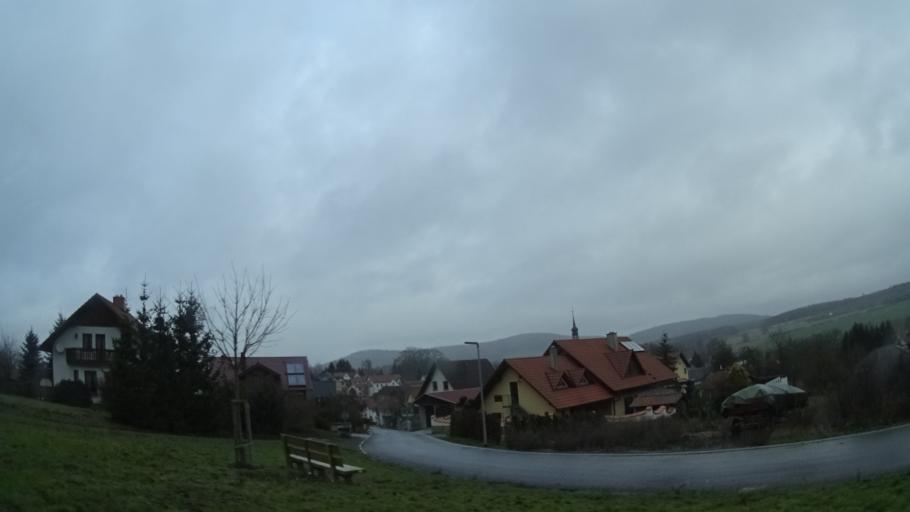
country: DE
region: Thuringia
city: Wolfershausen
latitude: 50.4682
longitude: 10.4351
